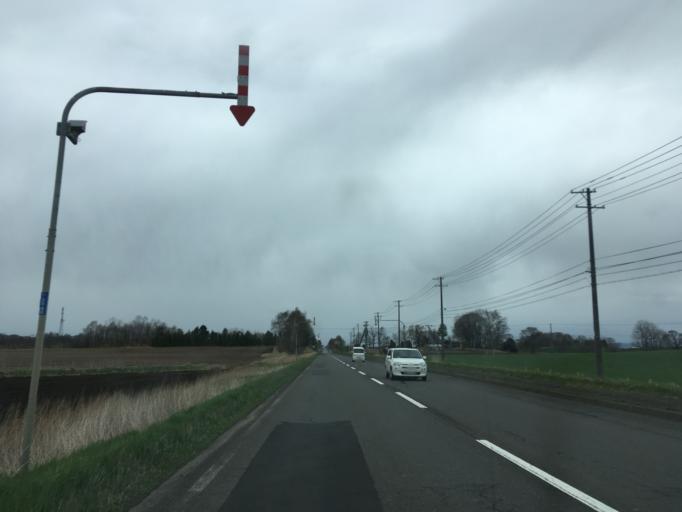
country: JP
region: Hokkaido
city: Chitose
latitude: 42.9101
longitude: 141.8114
